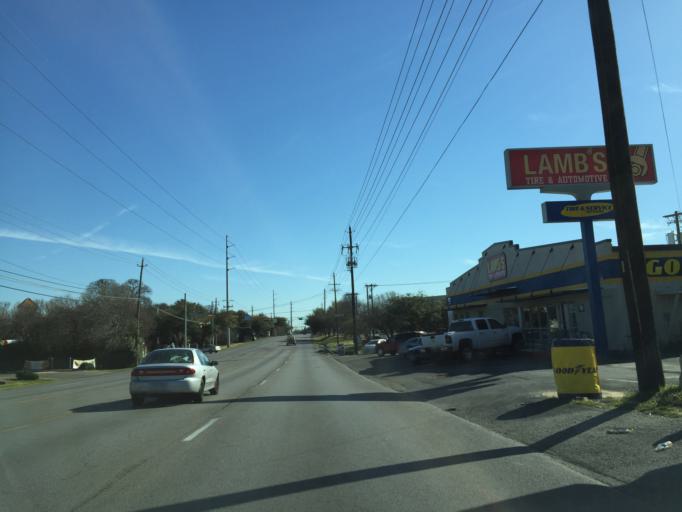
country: US
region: Texas
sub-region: Williamson County
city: Jollyville
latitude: 30.4377
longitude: -97.7592
